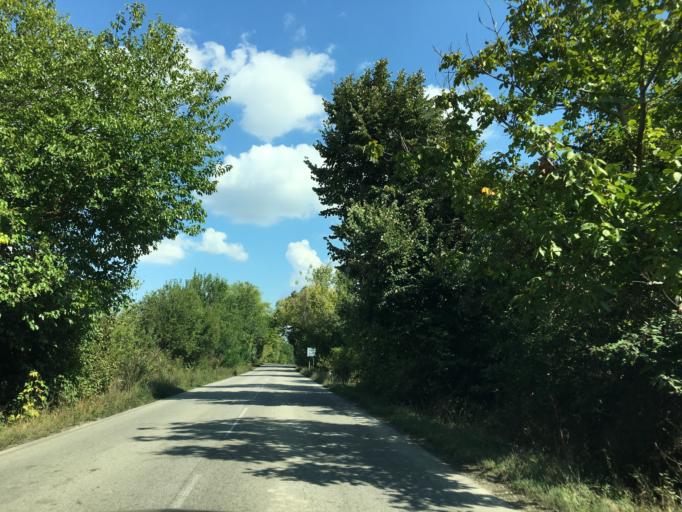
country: BG
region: Montana
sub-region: Obshtina Lom
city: Lom
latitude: 43.8177
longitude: 23.1885
